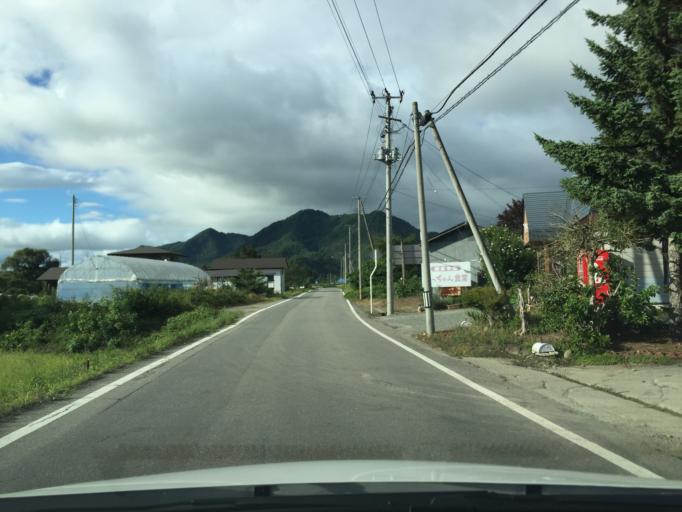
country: JP
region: Yamagata
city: Takahata
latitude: 37.9450
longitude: 140.2043
